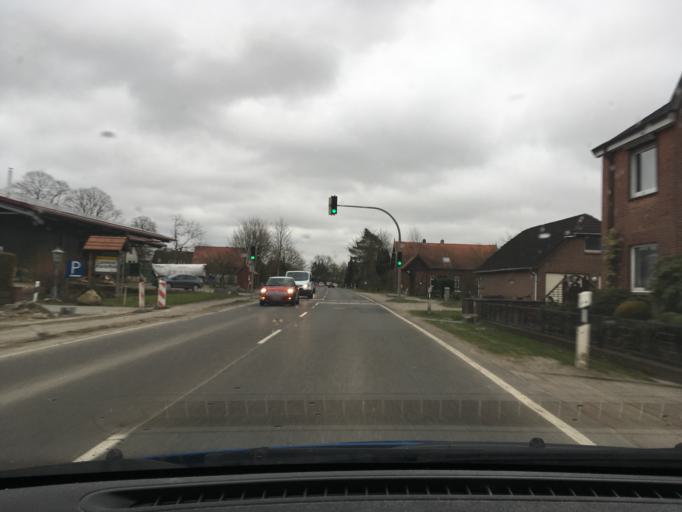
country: DE
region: Schleswig-Holstein
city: Escheburg
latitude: 53.4231
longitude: 10.3239
